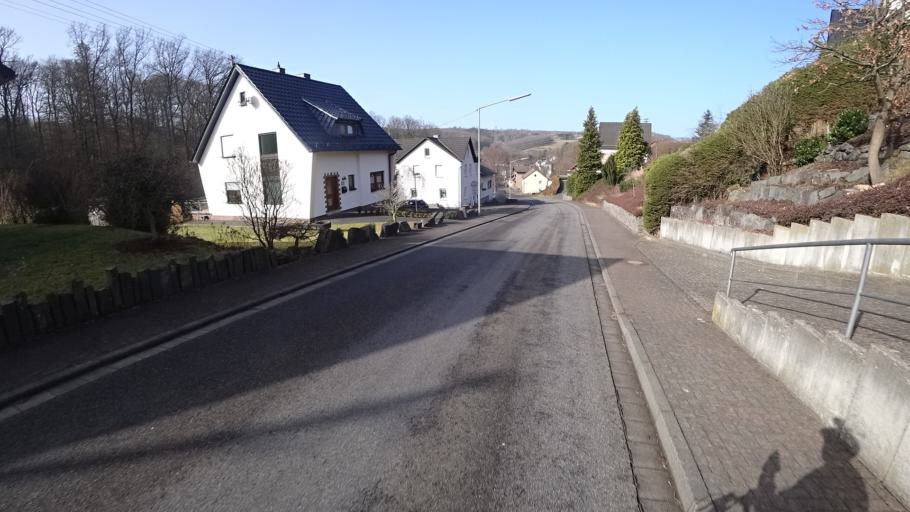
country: DE
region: Rheinland-Pfalz
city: Dickendorf
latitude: 50.7320
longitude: 7.8324
